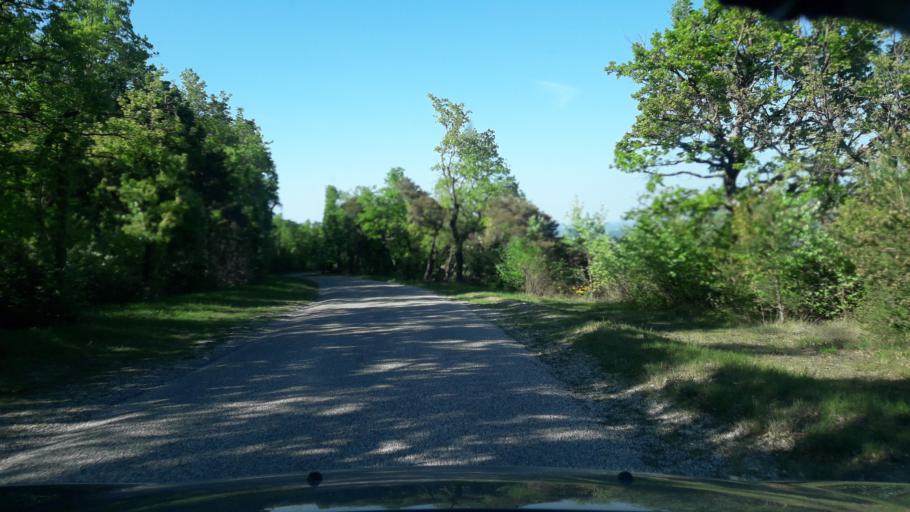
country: FR
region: Rhone-Alpes
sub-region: Departement de la Drome
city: Grane
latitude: 44.7106
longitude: 4.8897
